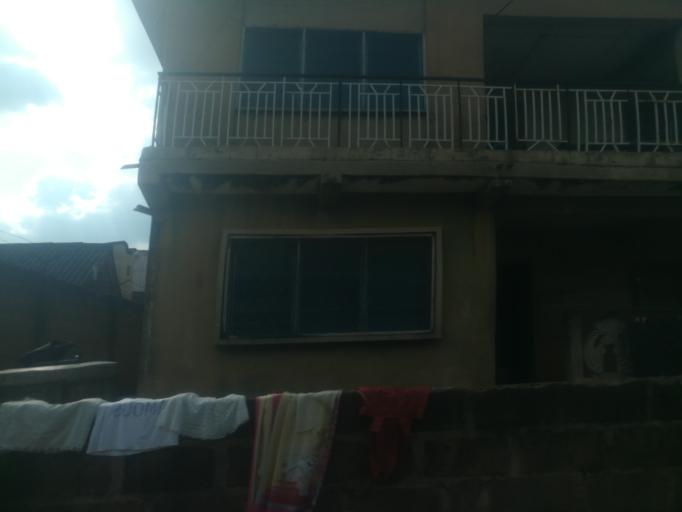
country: NG
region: Ogun
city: Abeokuta
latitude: 7.1184
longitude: 3.3303
